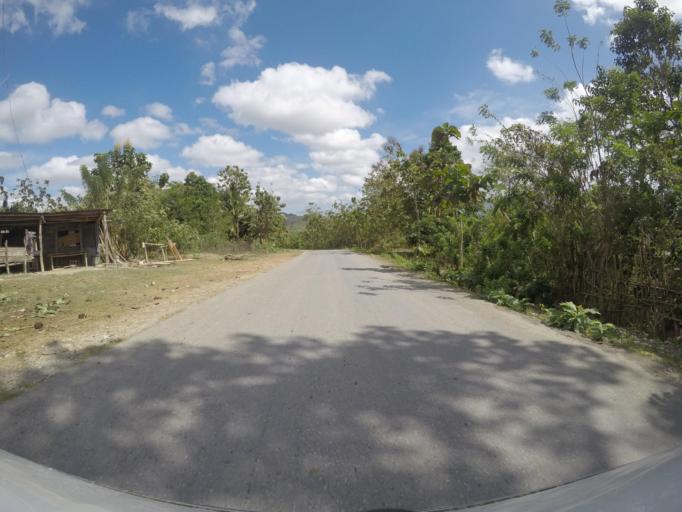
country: TL
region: Viqueque
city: Viqueque
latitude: -8.8716
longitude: 126.3550
